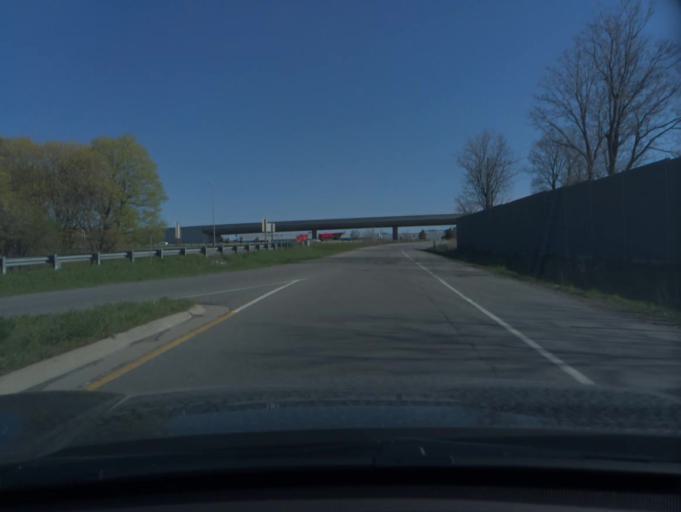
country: CA
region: Ontario
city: North Perth
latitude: 43.8026
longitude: -81.0002
